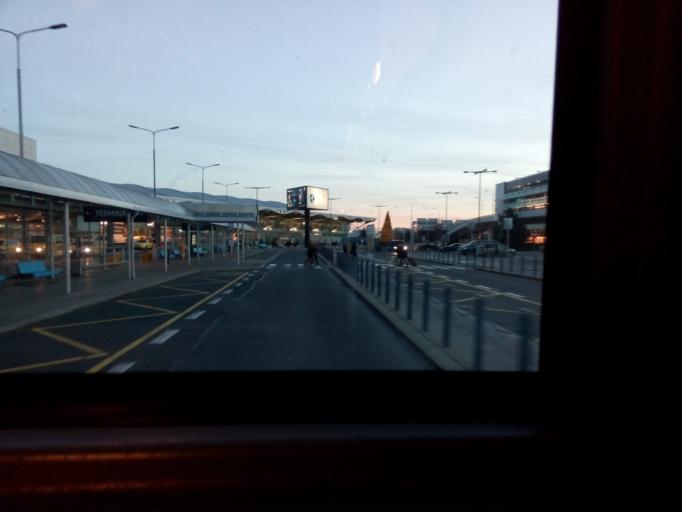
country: CZ
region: Central Bohemia
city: Hostivice
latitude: 50.1075
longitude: 14.2684
